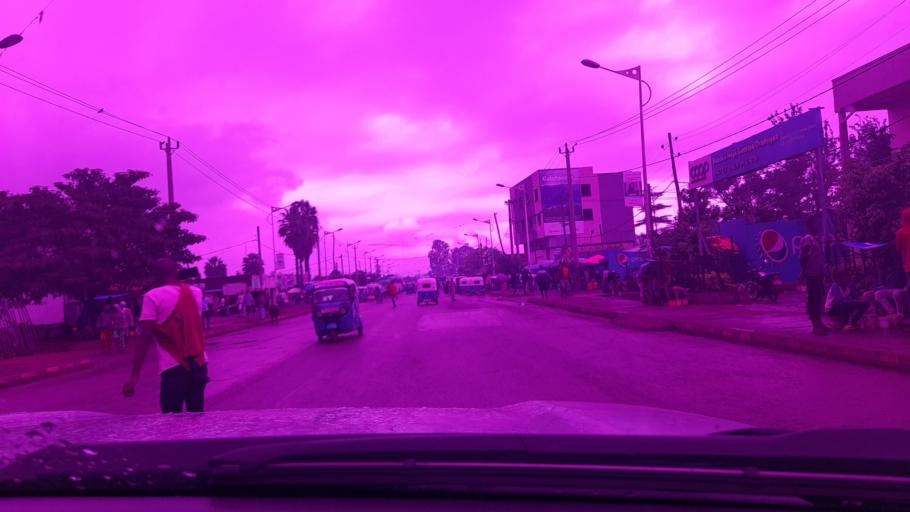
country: ET
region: Oromiya
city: Jima
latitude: 7.6664
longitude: 36.8403
